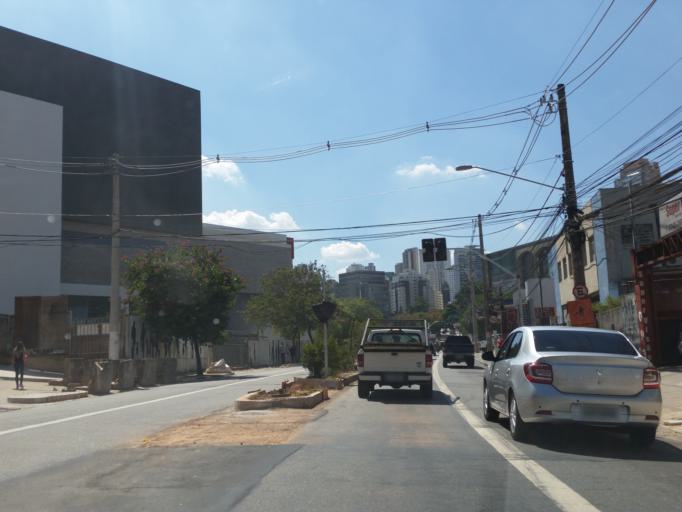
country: BR
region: Sao Paulo
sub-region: Taboao Da Serra
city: Taboao da Serra
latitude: -23.6331
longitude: -46.7370
